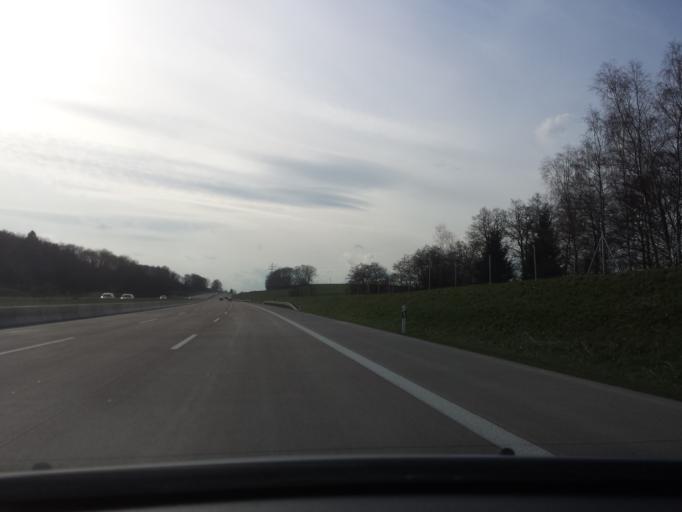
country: DE
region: Bavaria
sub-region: Swabia
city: Rettenbach
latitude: 48.4318
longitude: 10.3647
